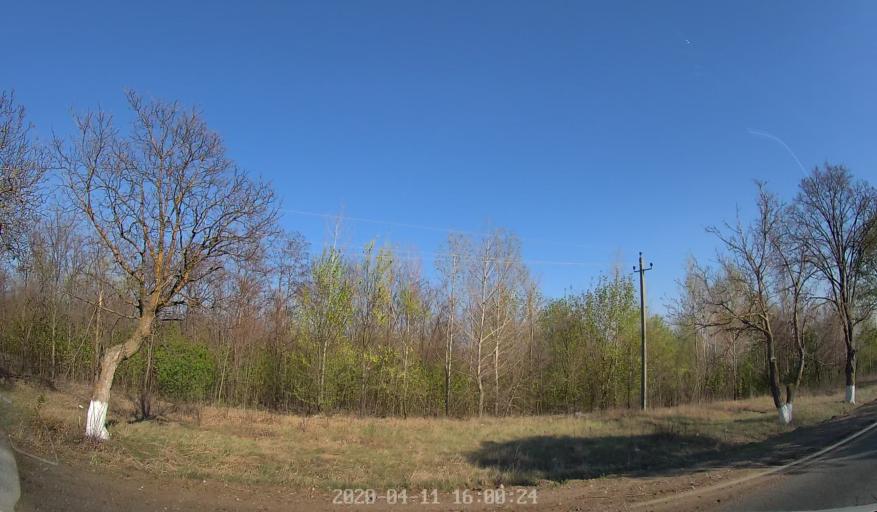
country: MD
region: Chisinau
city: Vadul lui Voda
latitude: 47.0768
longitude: 29.1361
